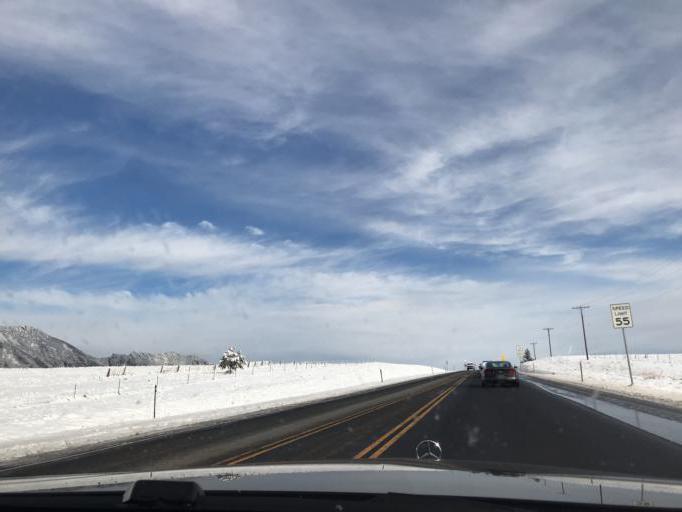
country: US
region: Colorado
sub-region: Boulder County
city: Superior
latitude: 39.9302
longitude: -105.2352
